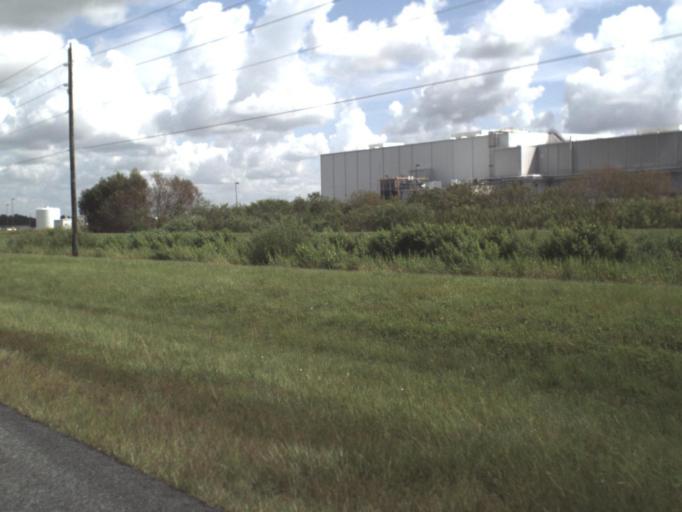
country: US
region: Florida
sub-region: Charlotte County
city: Harbour Heights
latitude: 27.0396
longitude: -81.9583
